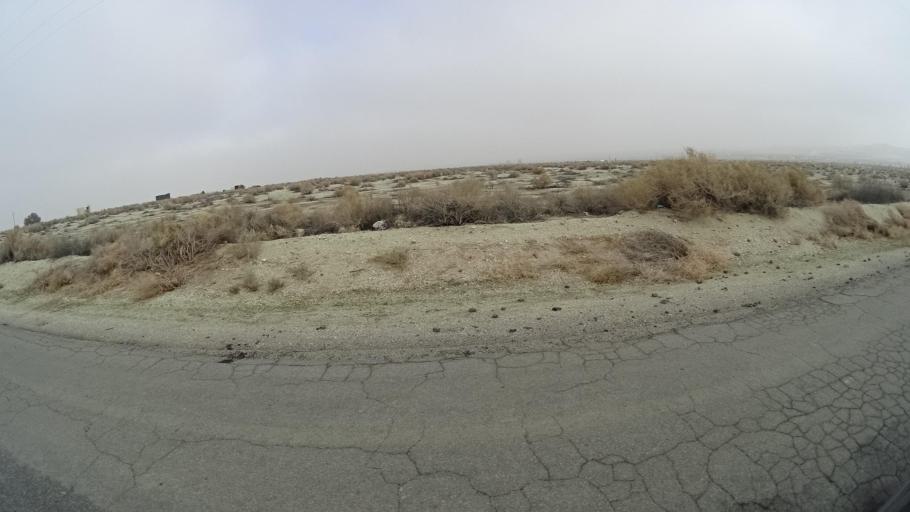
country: US
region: California
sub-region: Kern County
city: Maricopa
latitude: 35.0499
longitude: -119.3928
